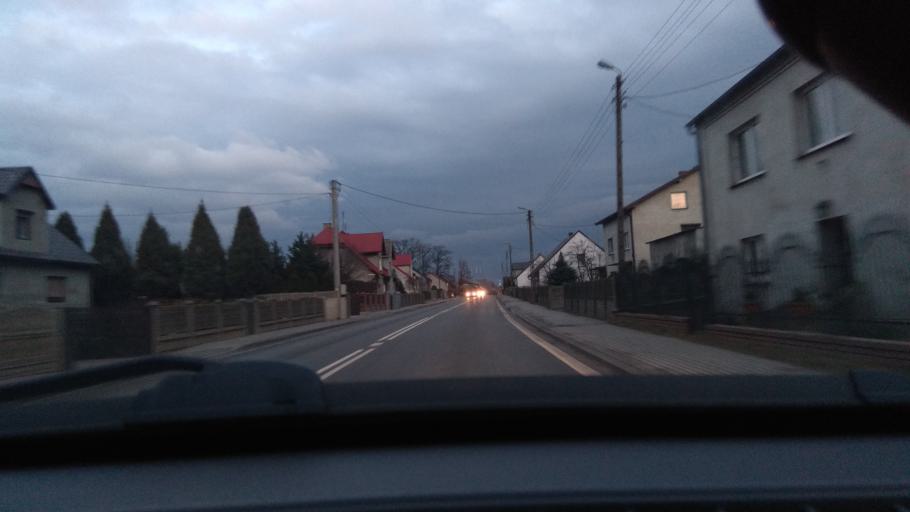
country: PL
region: Greater Poland Voivodeship
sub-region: Powiat kepinski
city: Baranow
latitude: 51.2951
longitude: 18.0389
